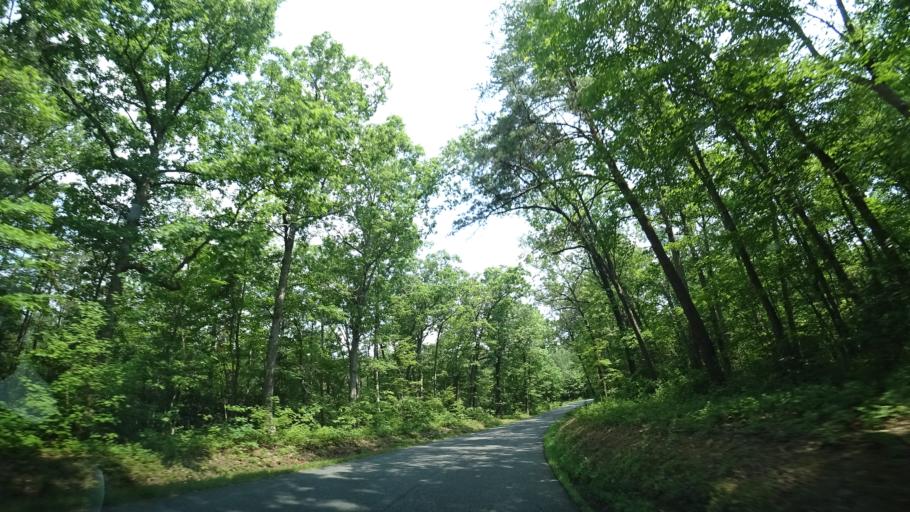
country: US
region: Virginia
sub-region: Spotsylvania County
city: Spotsylvania
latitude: 38.1275
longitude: -77.7889
